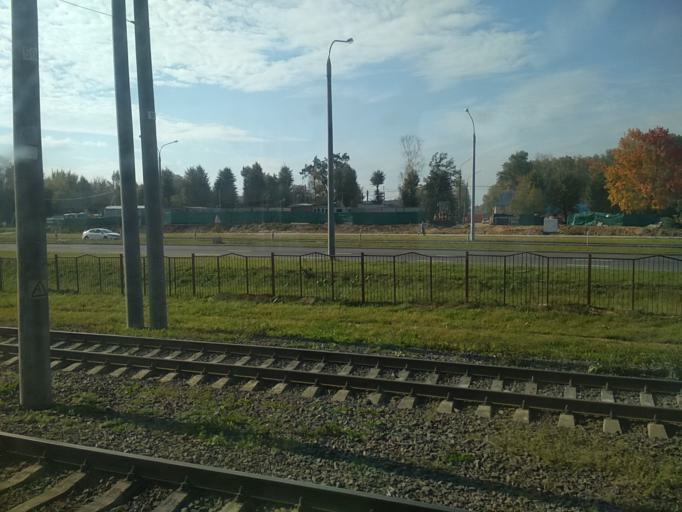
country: BY
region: Minsk
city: Minsk
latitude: 53.8677
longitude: 27.5610
